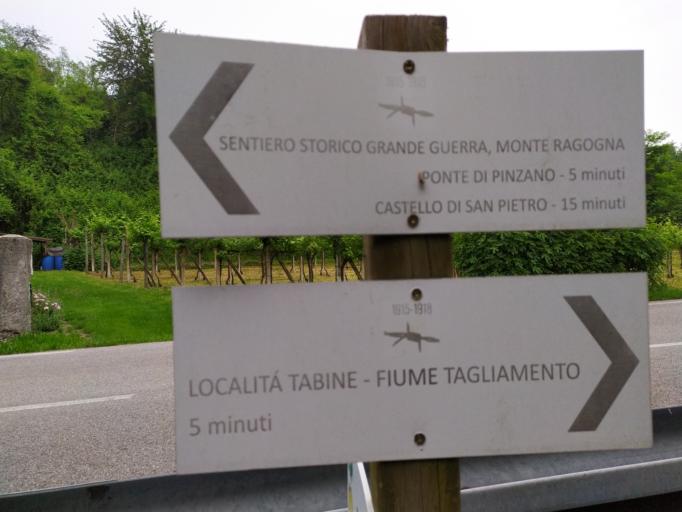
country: IT
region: Friuli Venezia Giulia
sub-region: Provincia di Pordenone
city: Pinzano al Tagliamento
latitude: 46.1810
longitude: 12.9594
